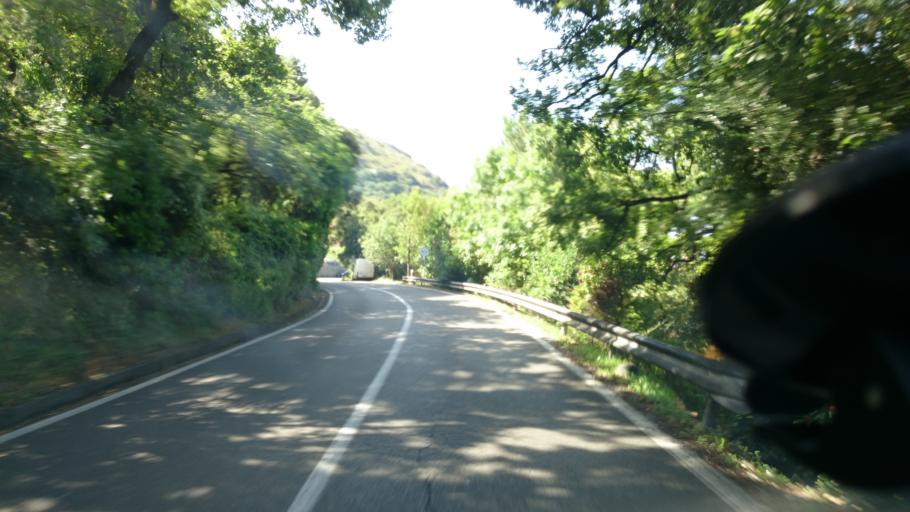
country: IT
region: Basilicate
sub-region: Provincia di Potenza
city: Maratea
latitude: 39.9972
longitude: 15.7128
